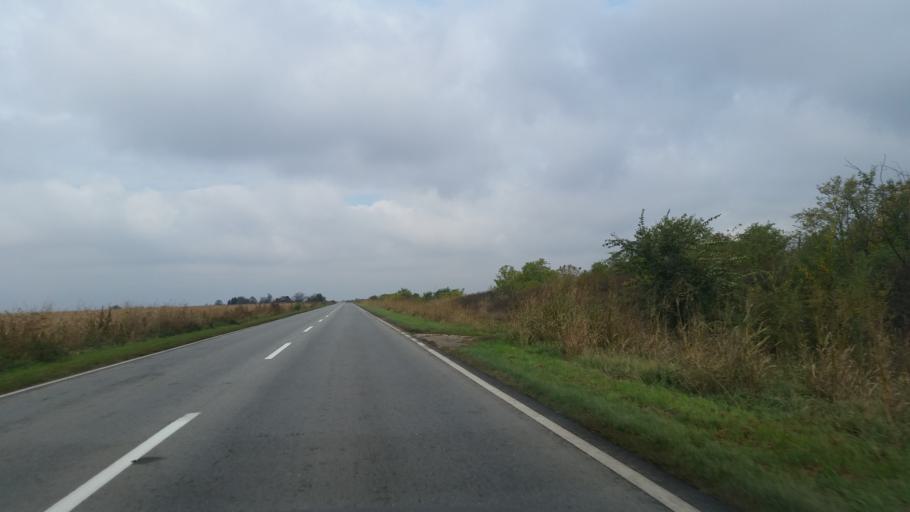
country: RS
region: Autonomna Pokrajina Vojvodina
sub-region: Srednjebanatski Okrug
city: Zrenjanin
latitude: 45.4407
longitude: 20.3629
